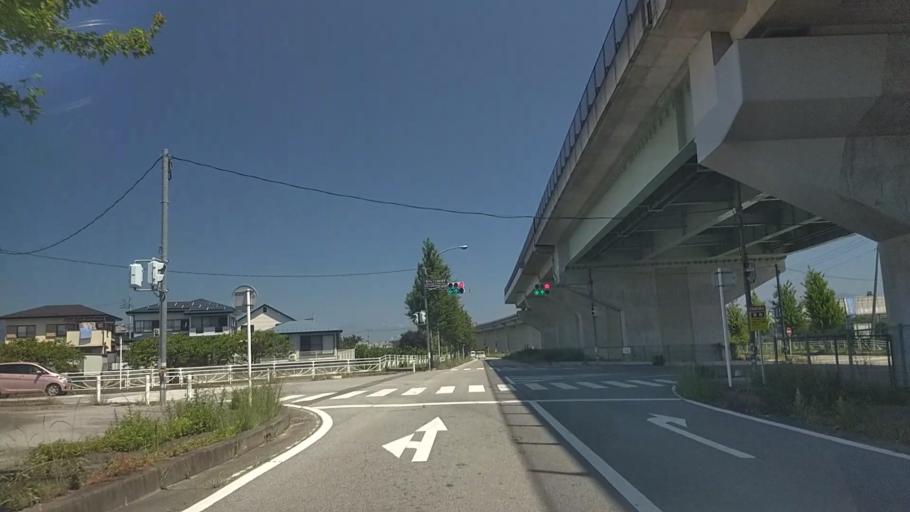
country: JP
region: Yamanashi
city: Ryuo
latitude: 35.6251
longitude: 138.4750
